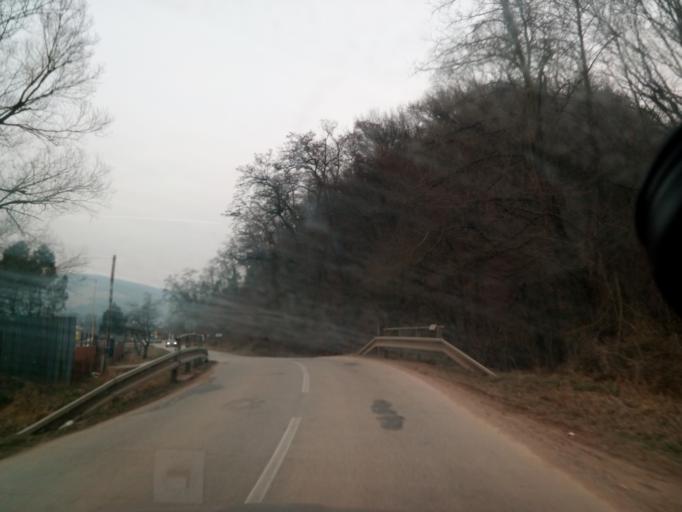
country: SK
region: Kosicky
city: Medzev
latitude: 48.6977
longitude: 20.9140
